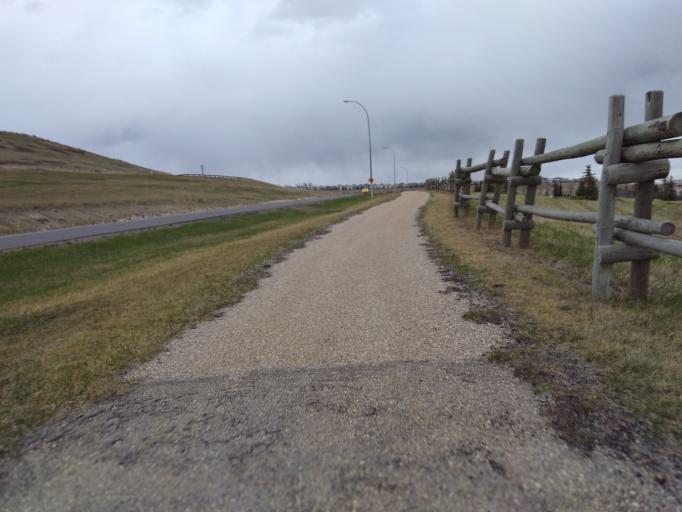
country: CA
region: Alberta
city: Cochrane
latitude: 51.1906
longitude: -114.4456
